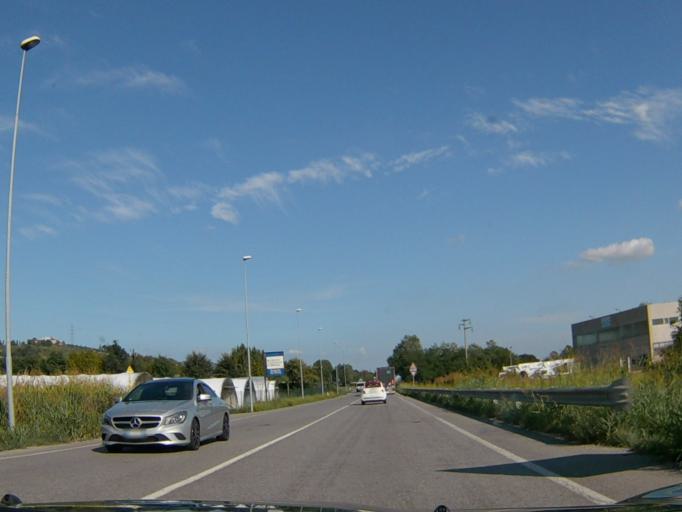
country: IT
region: Lombardy
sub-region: Provincia di Bergamo
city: Telgate
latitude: 45.6377
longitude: 9.8494
